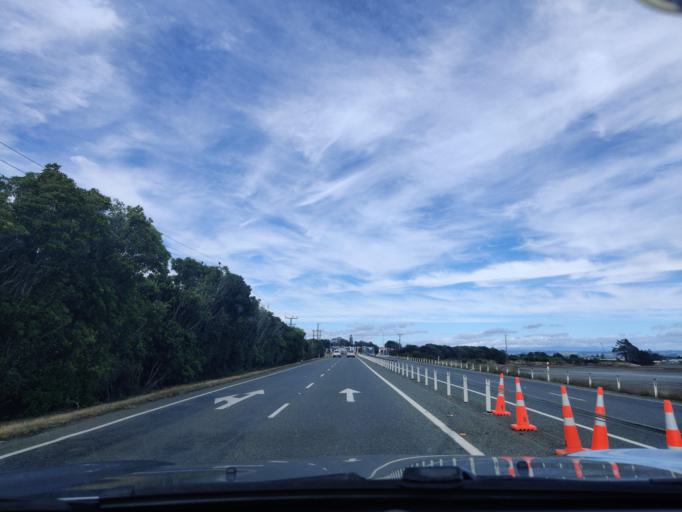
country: NZ
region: Tasman
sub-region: Tasman District
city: Richmond
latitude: -41.3293
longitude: 173.2054
